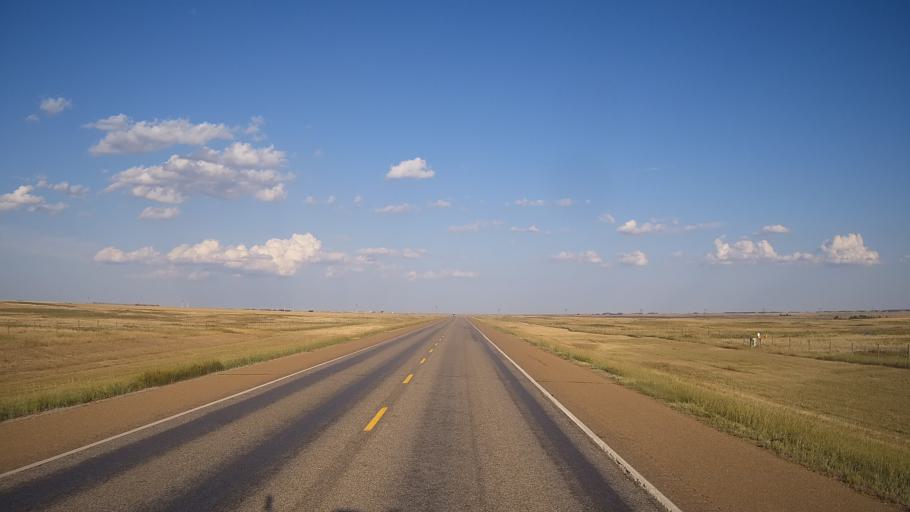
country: CA
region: Alberta
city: Hanna
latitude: 51.6241
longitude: -111.8790
